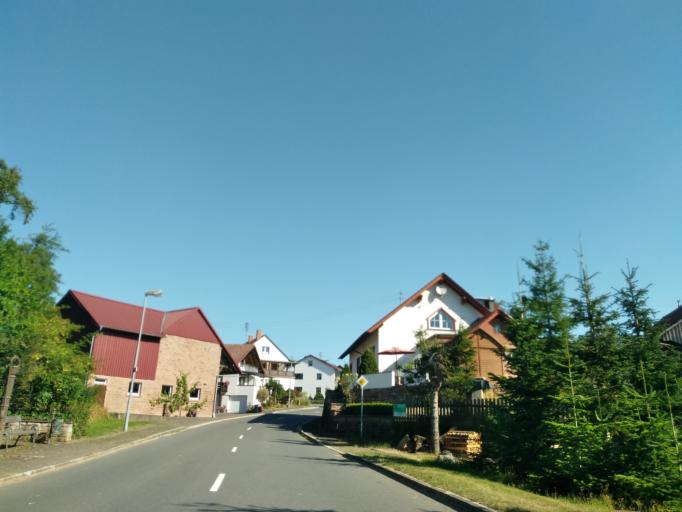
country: DE
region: Baden-Wuerttemberg
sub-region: Karlsruhe Region
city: Buchen
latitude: 49.5005
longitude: 9.2651
